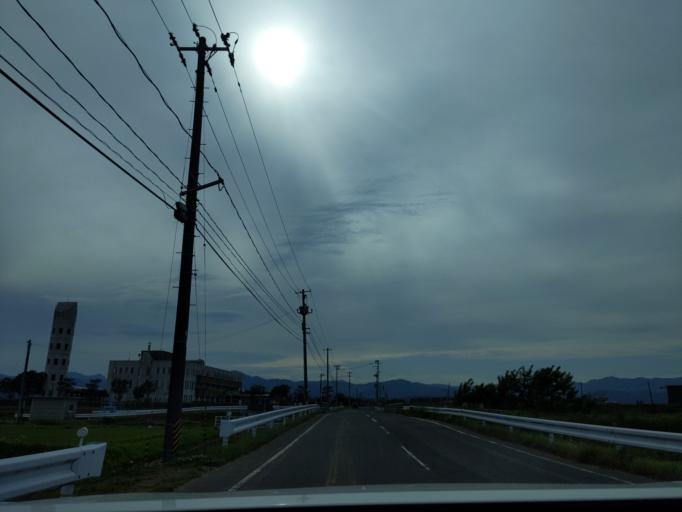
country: JP
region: Fukushima
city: Koriyama
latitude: 37.3757
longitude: 140.3199
